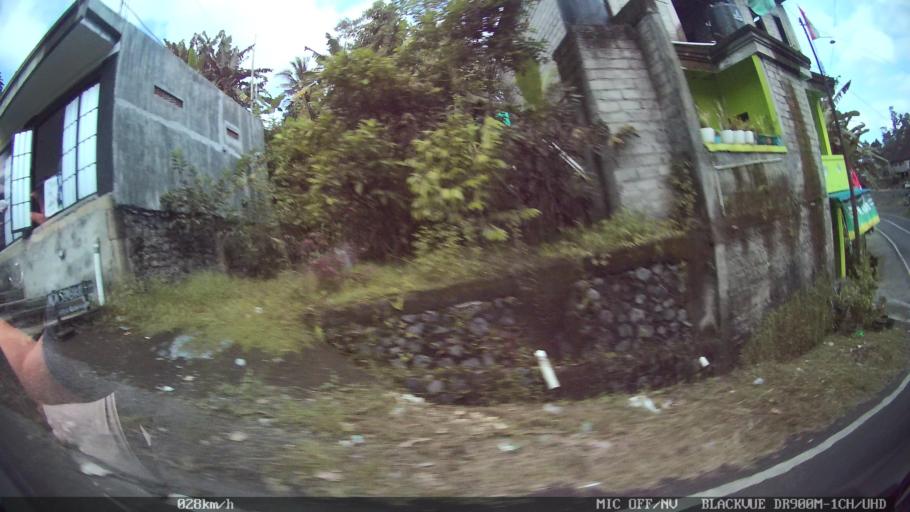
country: ID
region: Bali
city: Banjar Pesalakan
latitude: -8.5176
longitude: 115.3067
